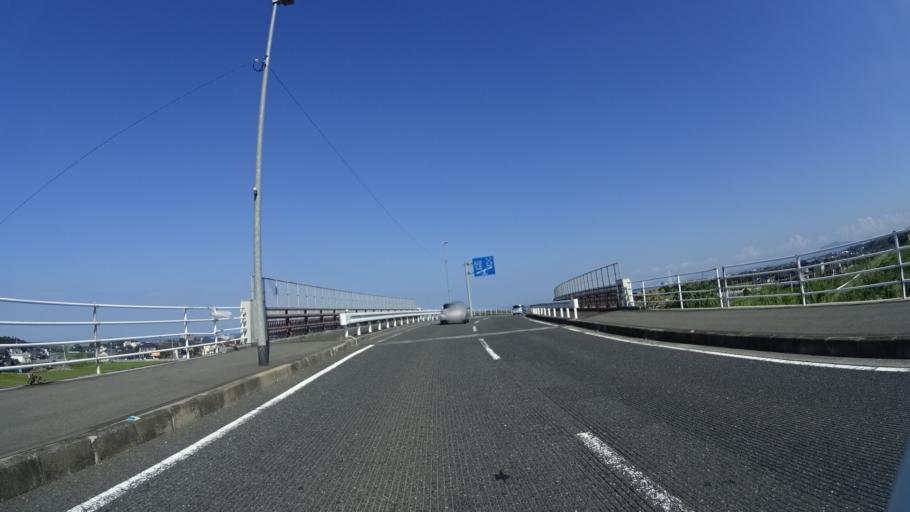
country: JP
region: Fukuoka
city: Shiida
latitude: 33.6459
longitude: 131.0652
